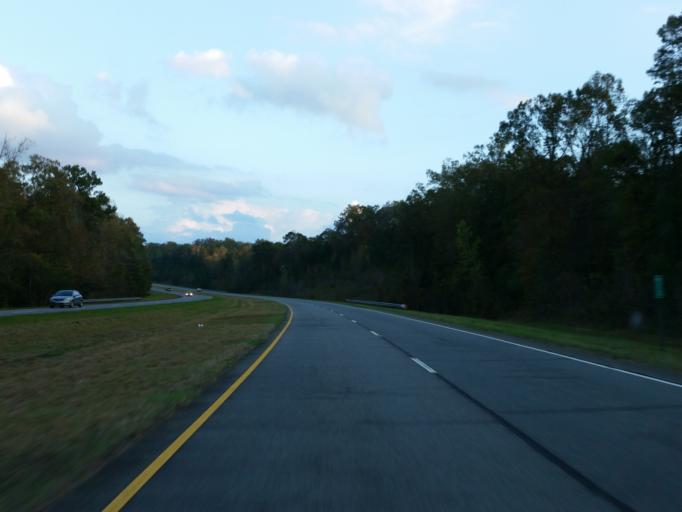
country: US
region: Georgia
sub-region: Houston County
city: Perry
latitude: 32.3988
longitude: -83.6420
